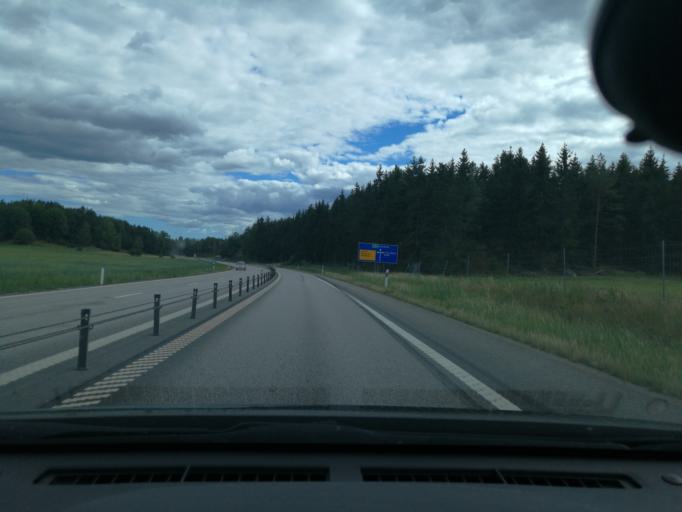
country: SE
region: OEstergoetland
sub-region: Soderkopings Kommun
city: Soederkoeping
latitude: 58.3874
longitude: 16.4108
